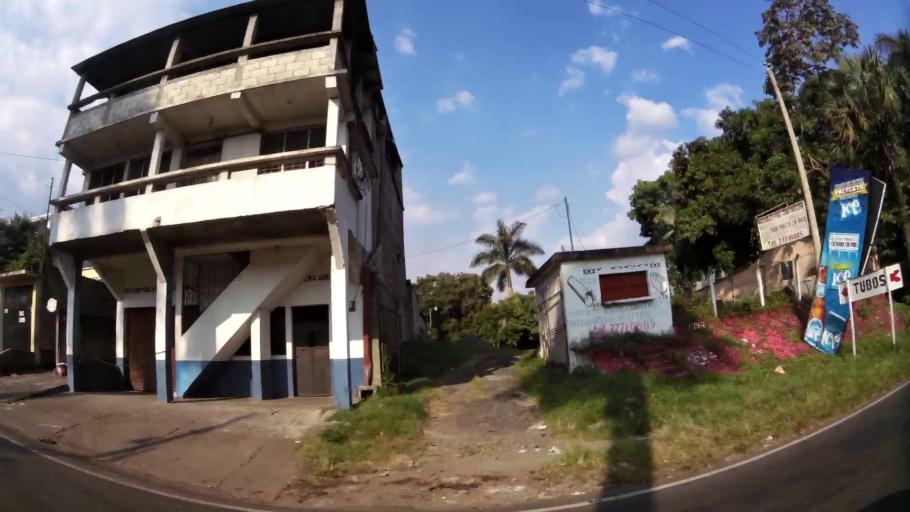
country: GT
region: Retalhuleu
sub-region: Municipio de Retalhuleu
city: Retalhuleu
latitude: 14.5323
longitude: -91.6789
